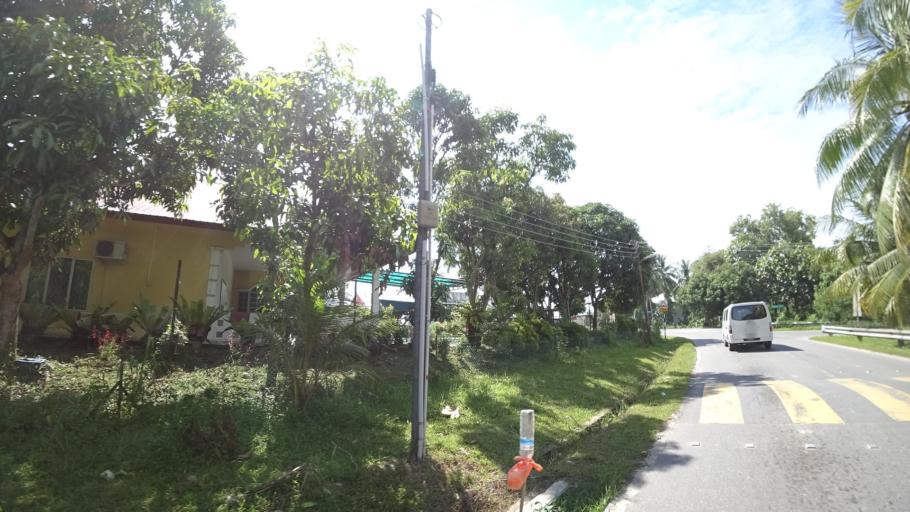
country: BN
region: Brunei and Muara
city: Bandar Seri Begawan
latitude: 4.8941
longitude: 114.8451
